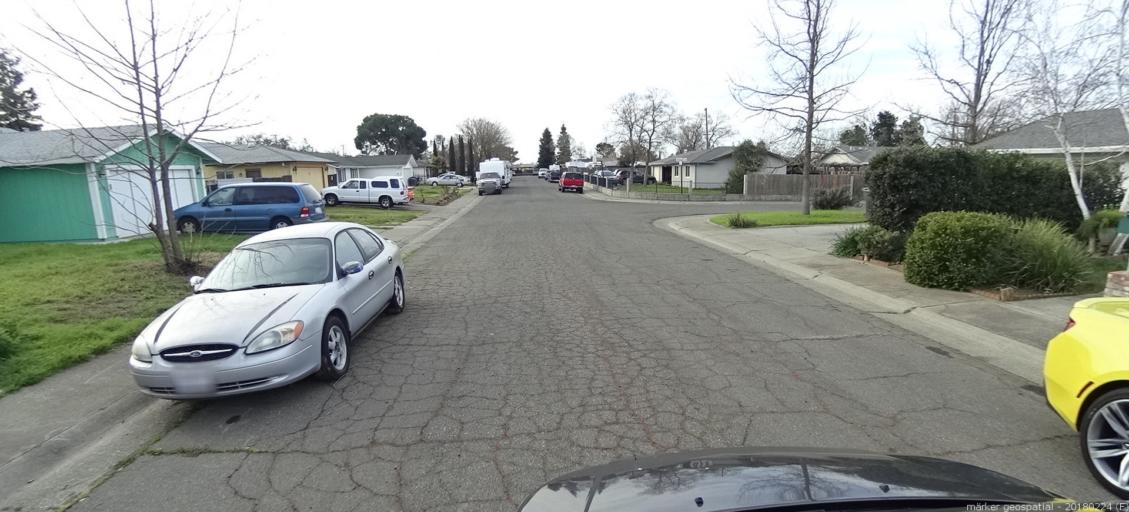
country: US
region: California
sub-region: Sacramento County
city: Rio Linda
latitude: 38.6794
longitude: -121.4676
